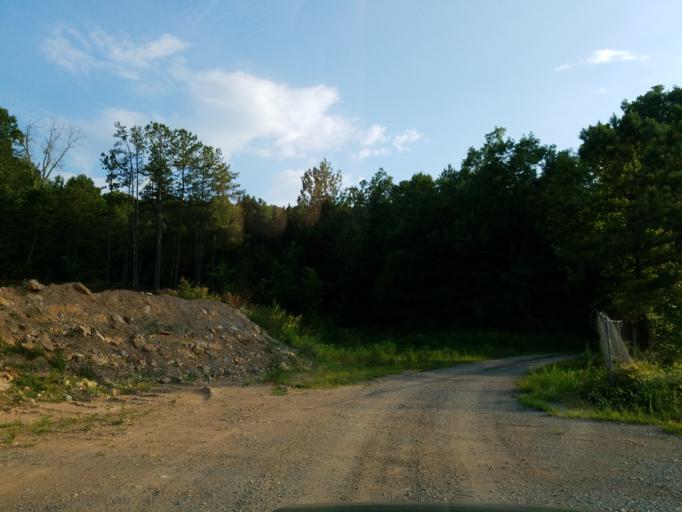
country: US
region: Georgia
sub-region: Gilmer County
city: Ellijay
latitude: 34.6561
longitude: -84.4429
